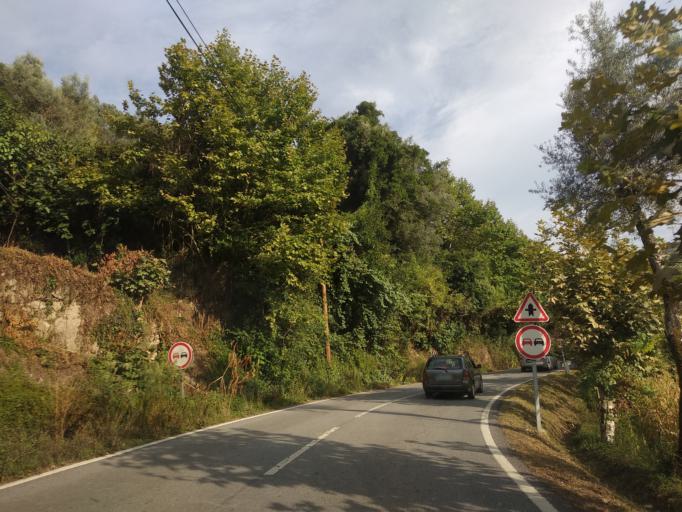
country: PT
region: Braga
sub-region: Vieira do Minho
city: Real
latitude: 41.6669
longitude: -8.1786
